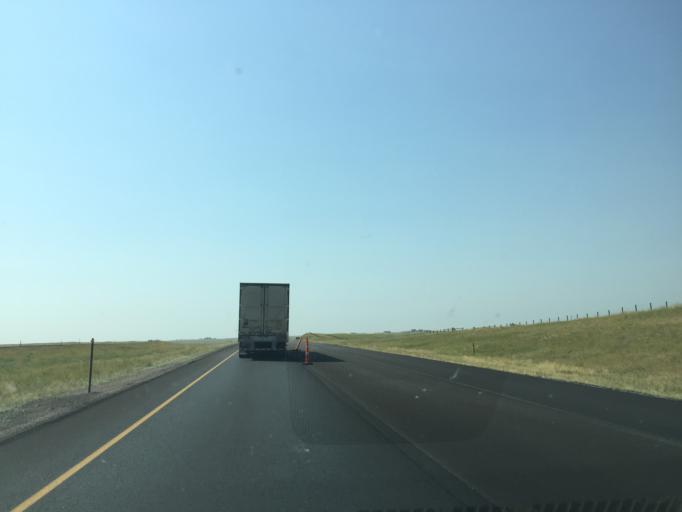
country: US
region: Wyoming
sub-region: Laramie County
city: Ranchettes
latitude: 41.3179
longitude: -104.8601
